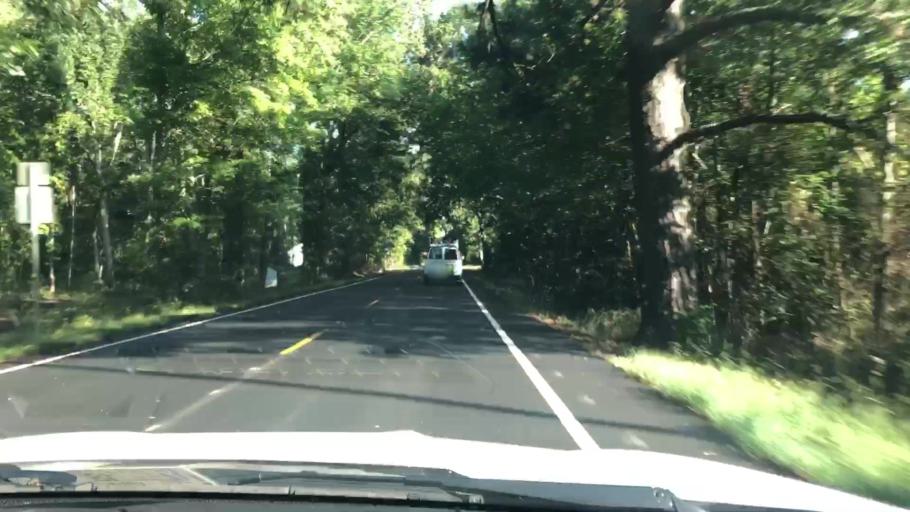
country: US
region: Virginia
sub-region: King William County
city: West Point
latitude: 37.4681
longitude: -76.8439
